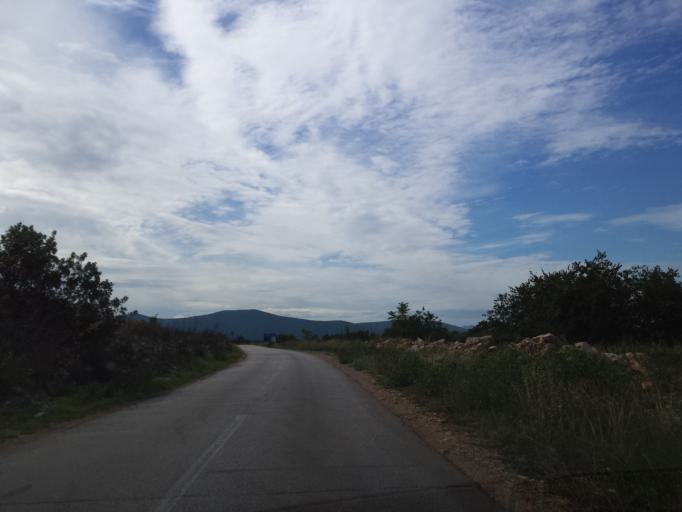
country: BA
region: Federation of Bosnia and Herzegovina
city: Citluk
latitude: 43.1857
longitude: 17.6476
